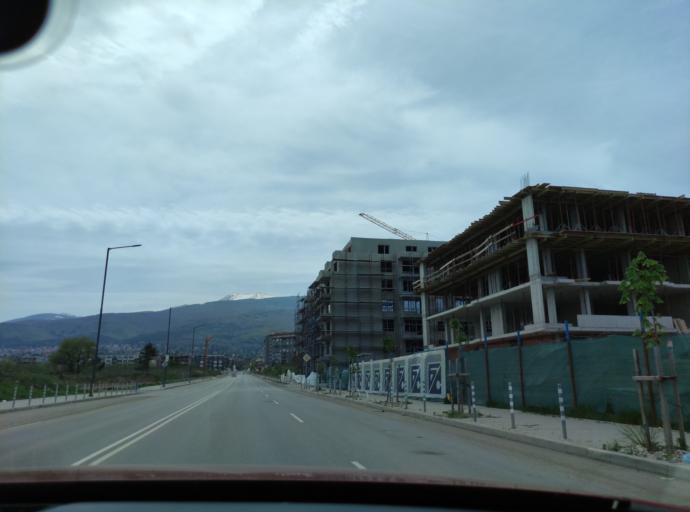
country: BG
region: Sofia-Capital
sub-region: Stolichna Obshtina
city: Sofia
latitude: 42.6408
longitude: 23.3440
